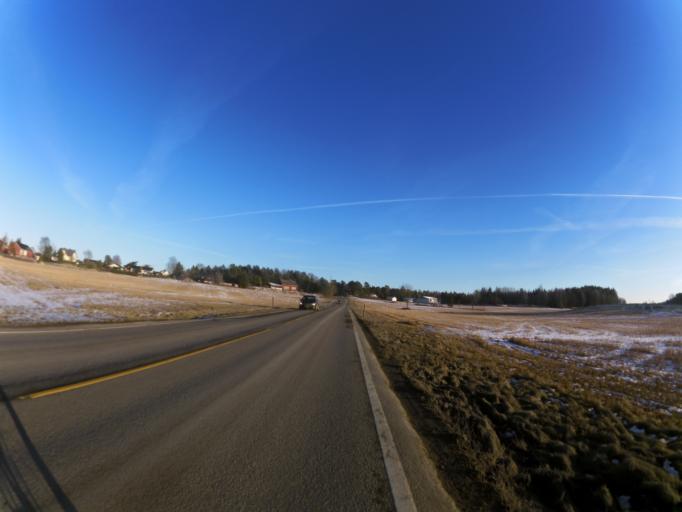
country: NO
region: Ostfold
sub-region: Fredrikstad
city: Lervik
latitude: 59.2628
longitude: 10.8136
